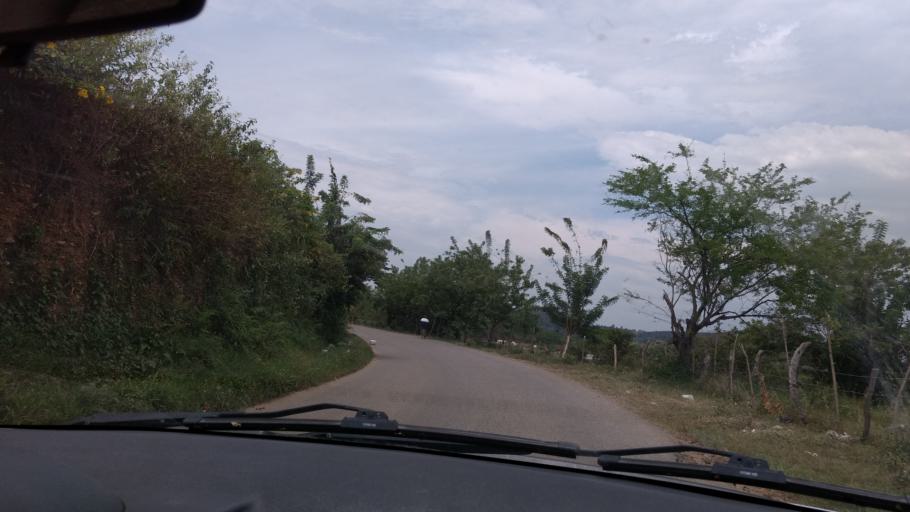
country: CO
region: Cauca
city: Buenos Aires
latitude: 3.1117
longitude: -76.6256
